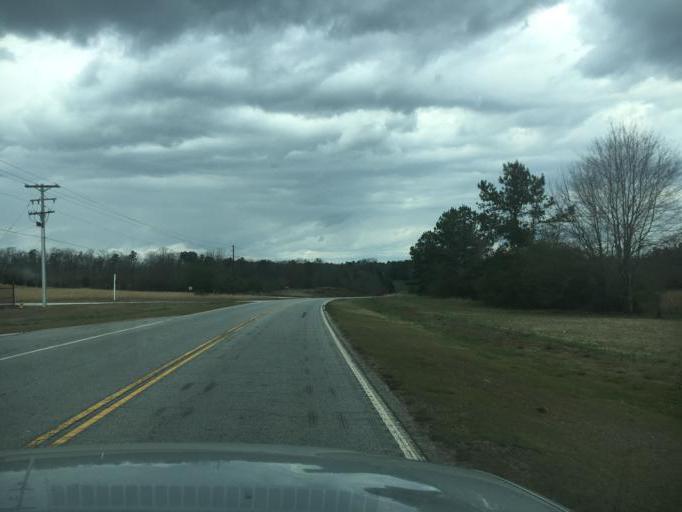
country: US
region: South Carolina
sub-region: Oconee County
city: Walhalla
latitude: 34.7247
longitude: -83.0561
